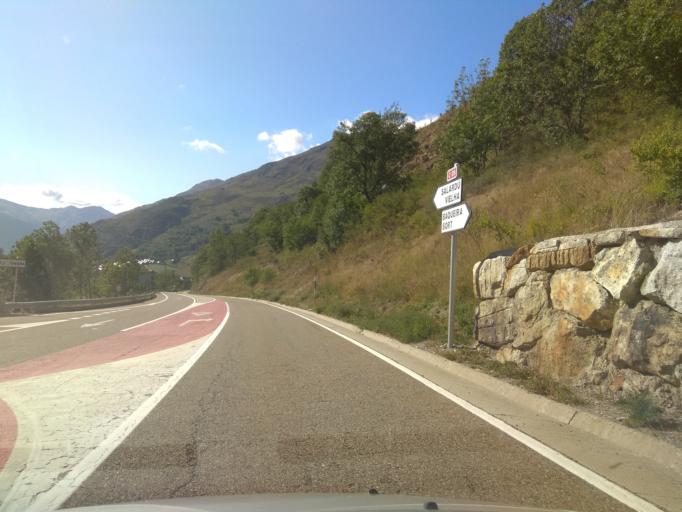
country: ES
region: Catalonia
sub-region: Provincia de Lleida
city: Vielha
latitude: 42.7065
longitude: 0.9037
